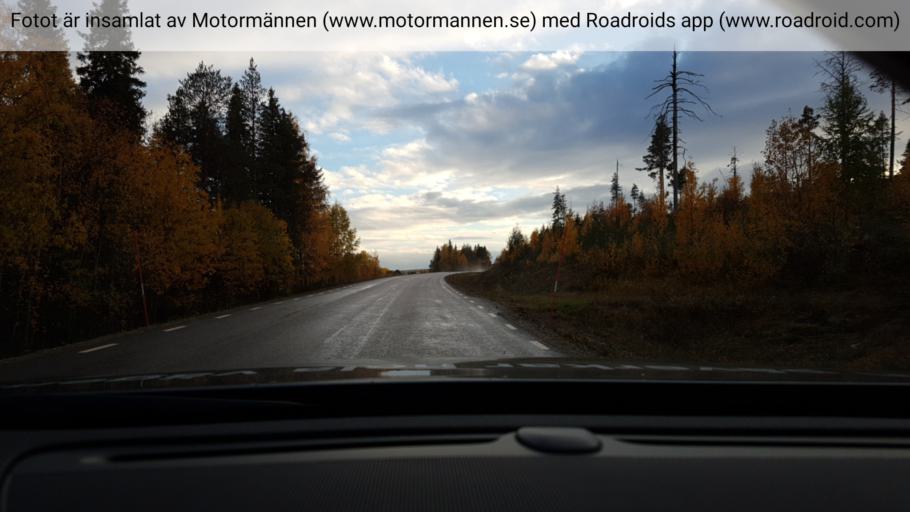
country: SE
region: Norrbotten
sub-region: Overkalix Kommun
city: OEverkalix
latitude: 66.7709
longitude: 22.6905
